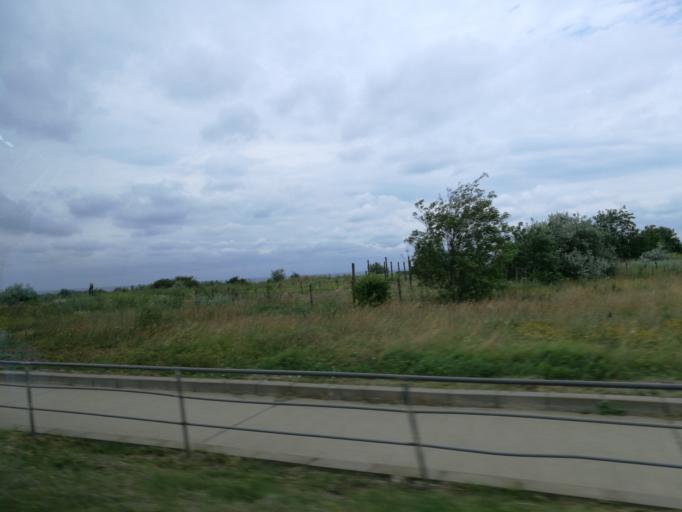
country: RO
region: Constanta
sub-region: Municipiul Mangalia
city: Mangalia
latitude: 43.7642
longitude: 28.5739
